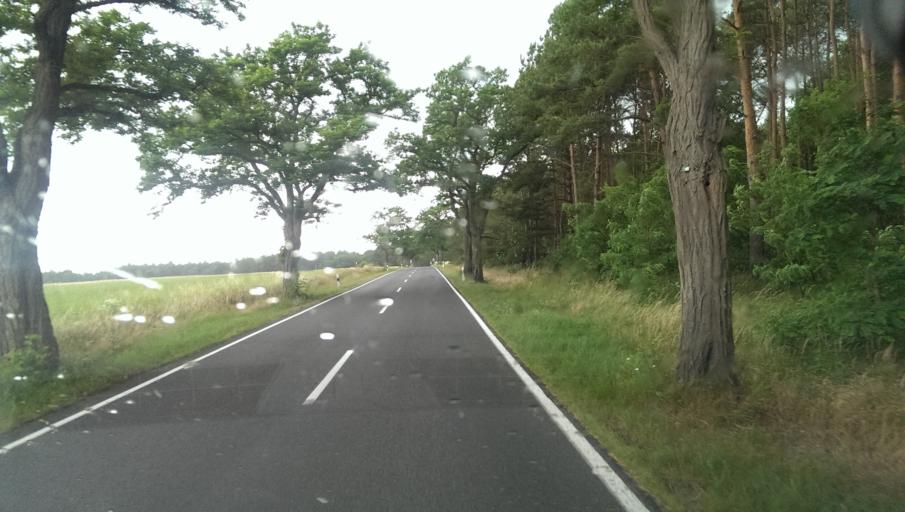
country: DE
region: Brandenburg
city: Borkwalde
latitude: 52.2974
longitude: 12.8083
